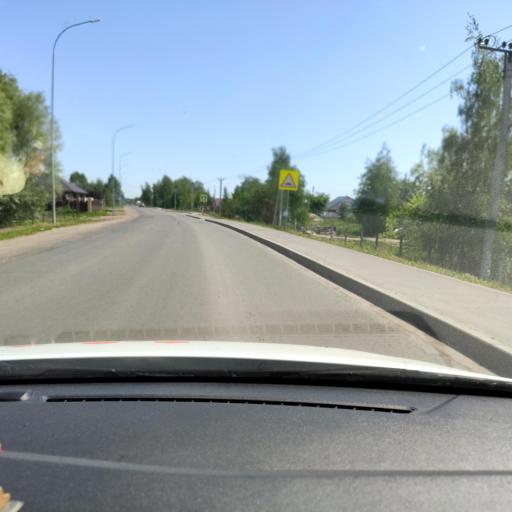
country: RU
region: Tatarstan
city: Stolbishchi
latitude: 55.6944
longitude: 49.2011
